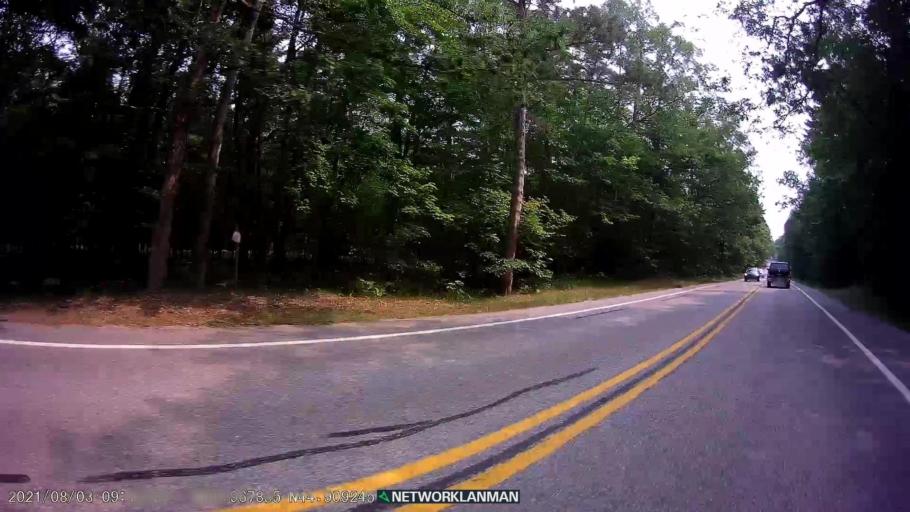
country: US
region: Michigan
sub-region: Leelanau County
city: Leland
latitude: 44.9093
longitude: -85.9671
